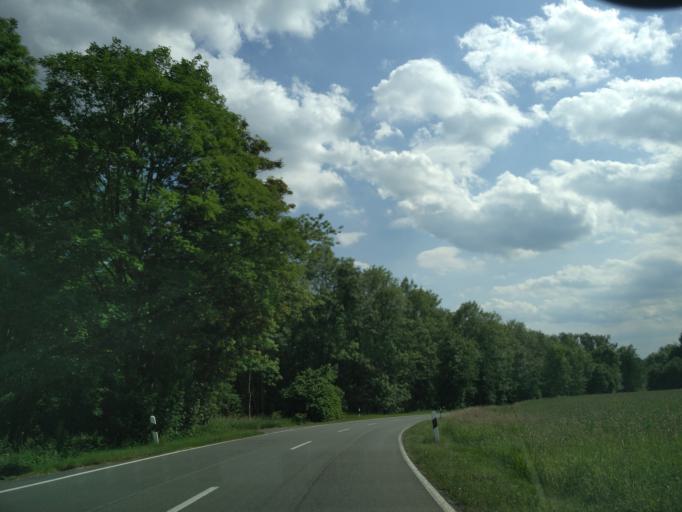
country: DE
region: North Rhine-Westphalia
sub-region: Regierungsbezirk Detmold
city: Willebadessen
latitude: 51.6454
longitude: 9.0454
